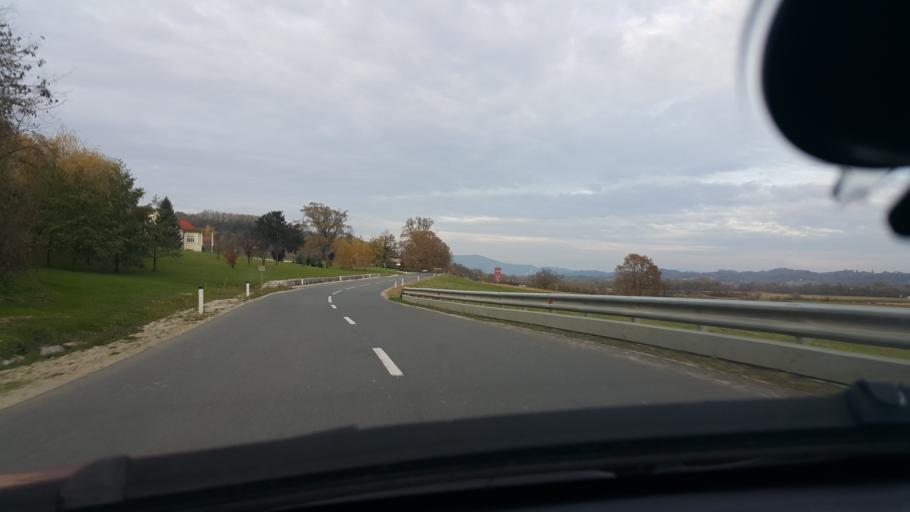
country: SI
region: Bistrica ob Sotli
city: Bistrica ob Sotli
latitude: 45.9680
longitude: 15.6940
